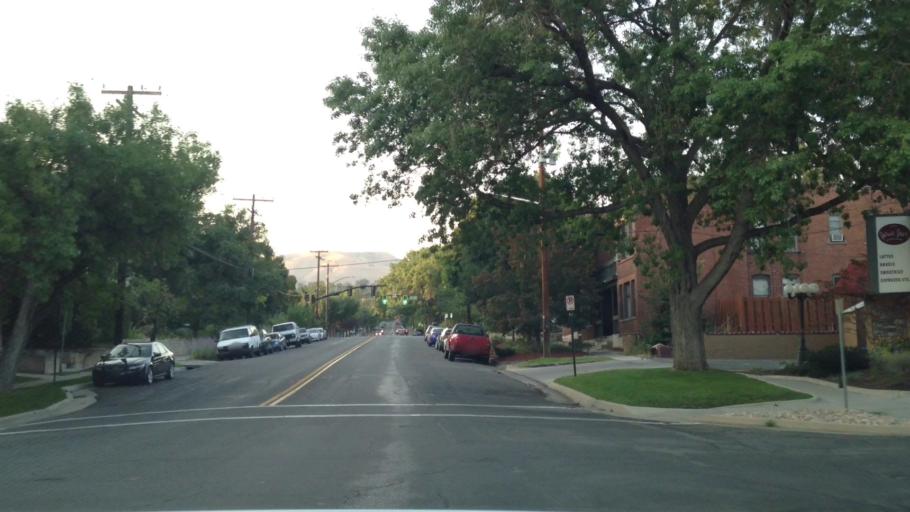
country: US
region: Utah
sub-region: Salt Lake County
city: Salt Lake City
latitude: 40.7704
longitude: -111.8775
